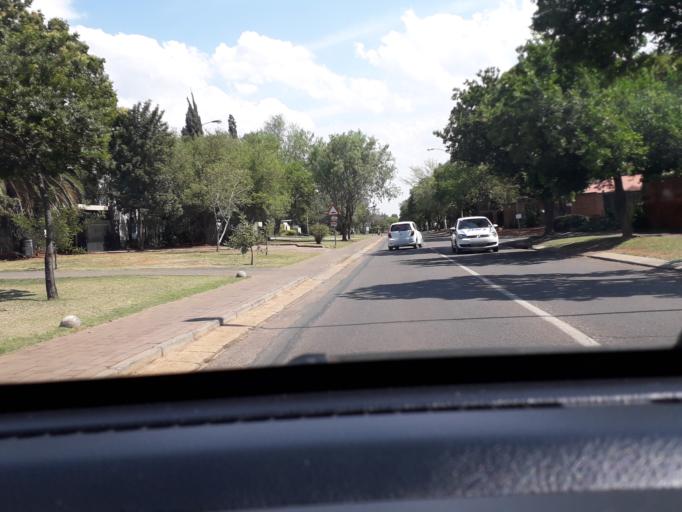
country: ZA
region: Gauteng
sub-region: City of Tshwane Metropolitan Municipality
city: Centurion
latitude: -25.8402
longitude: 28.2388
